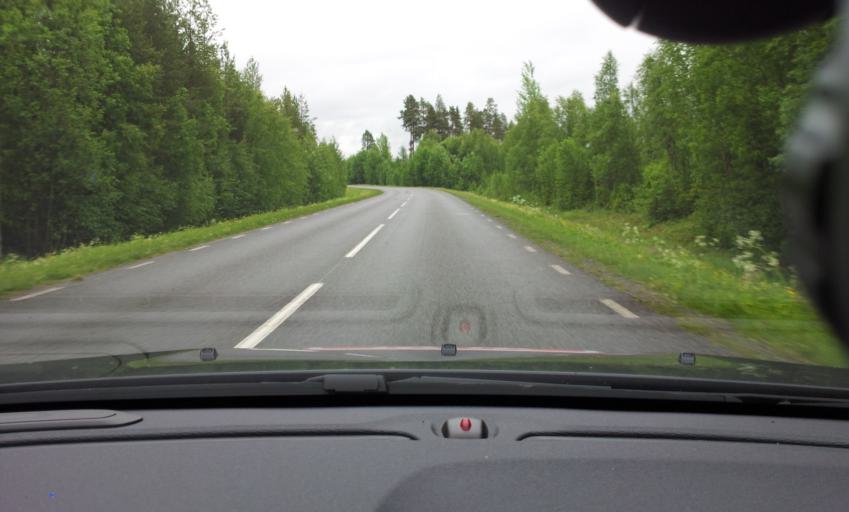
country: SE
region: Jaemtland
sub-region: Stroemsunds Kommun
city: Stroemsund
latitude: 63.5992
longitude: 15.3095
